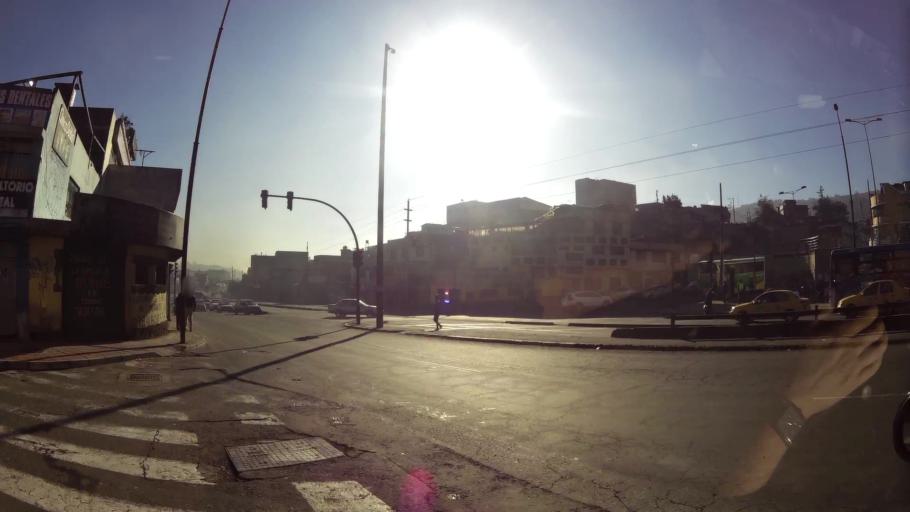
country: EC
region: Pichincha
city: Quito
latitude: -0.2426
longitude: -78.5130
